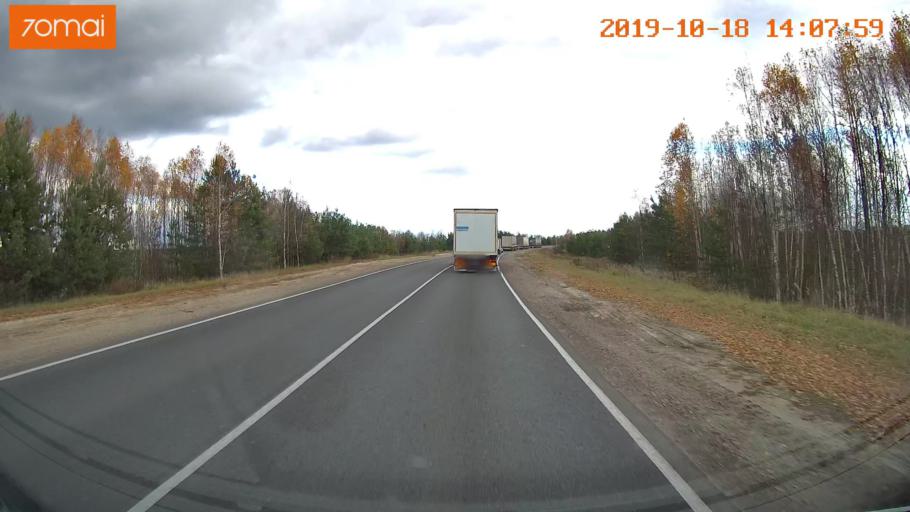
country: RU
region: Rjazan
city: Spas-Klepiki
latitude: 55.1517
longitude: 40.1667
